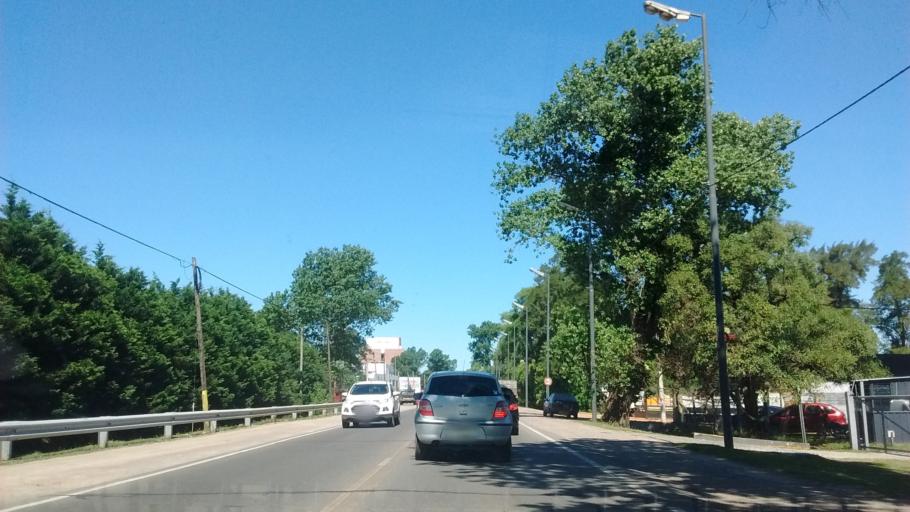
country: AR
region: Santa Fe
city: Funes
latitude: -32.9262
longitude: -60.7545
